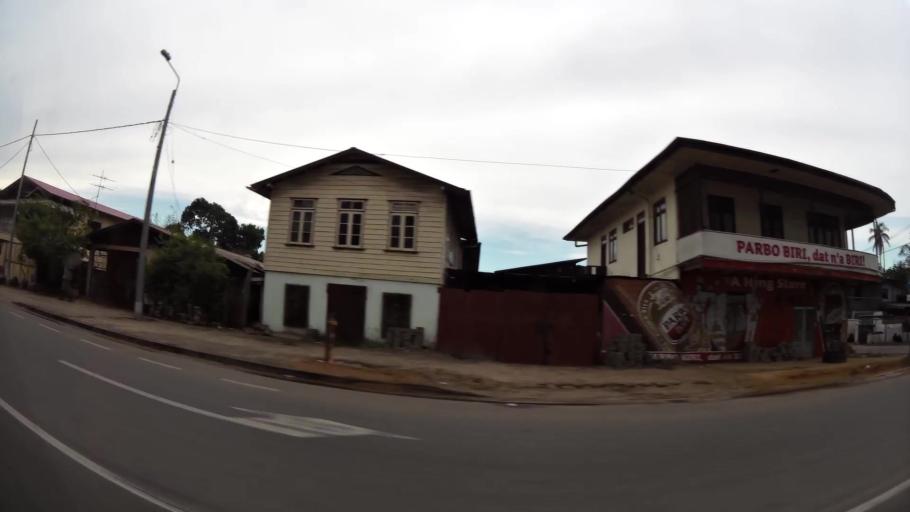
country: SR
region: Paramaribo
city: Paramaribo
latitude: 5.8053
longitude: -55.1799
